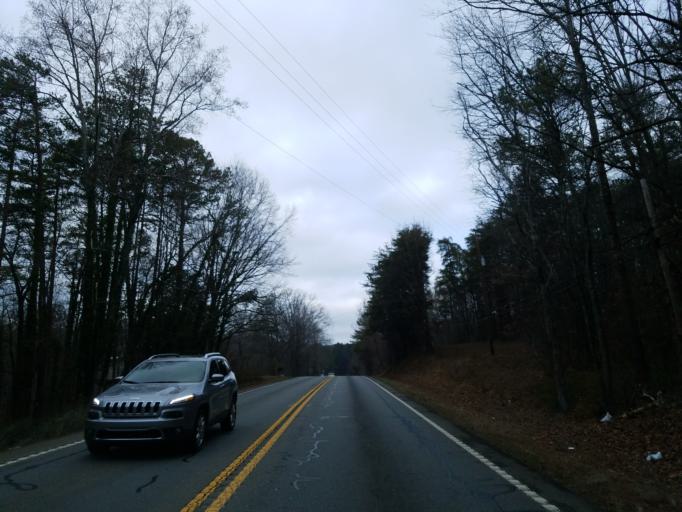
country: US
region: Georgia
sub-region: Cherokee County
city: Canton
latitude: 34.2637
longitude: -84.4939
